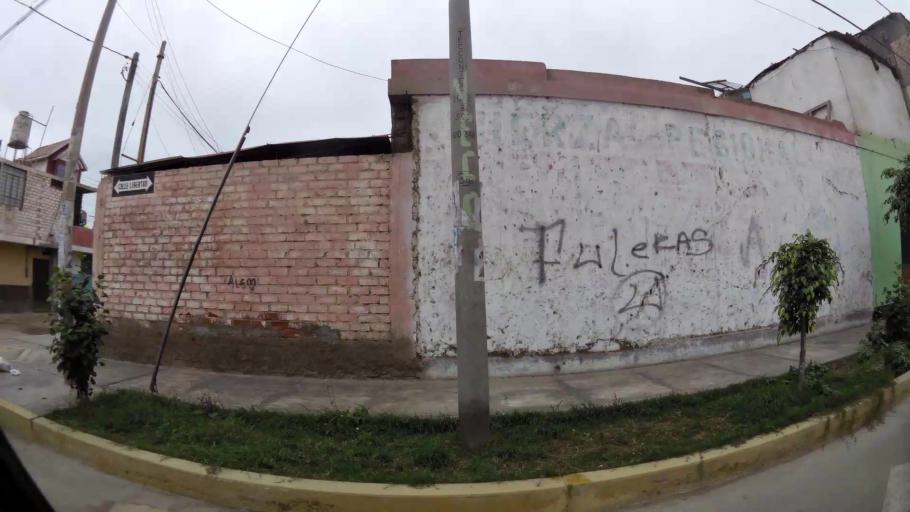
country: PE
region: Lima
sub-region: Barranca
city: Paramonga
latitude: -10.6741
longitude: -77.8155
